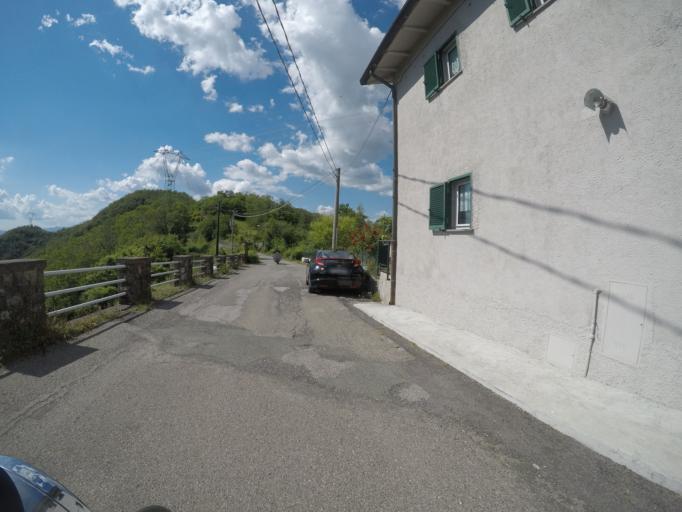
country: IT
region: Tuscany
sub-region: Provincia di Massa-Carrara
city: Casola in Lunigiana
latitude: 44.1768
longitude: 10.1810
